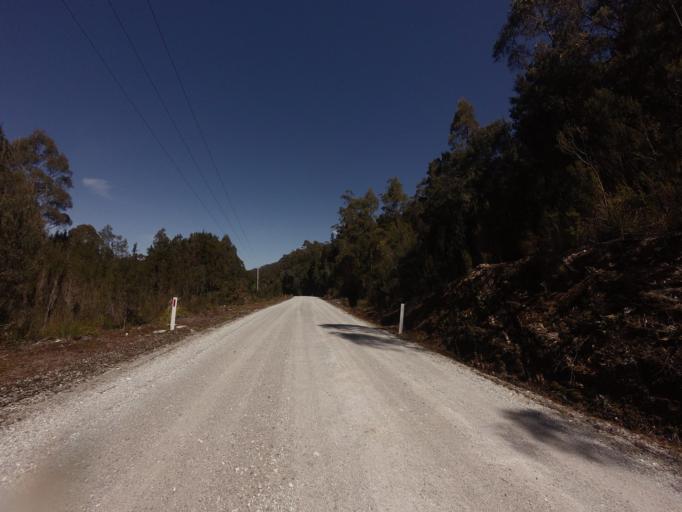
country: AU
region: Tasmania
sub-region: West Coast
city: Queenstown
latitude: -42.7582
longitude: 145.9856
